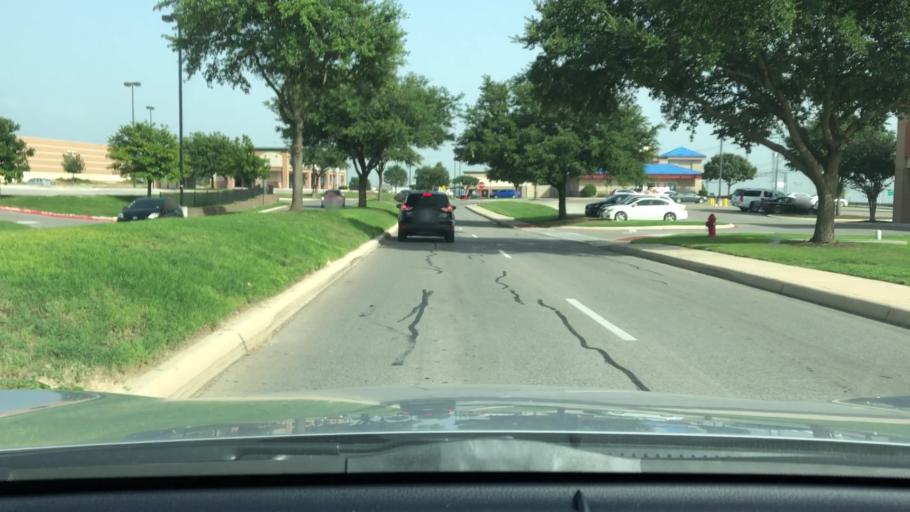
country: US
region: Texas
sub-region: Bexar County
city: Live Oak
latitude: 29.5642
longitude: -98.3287
